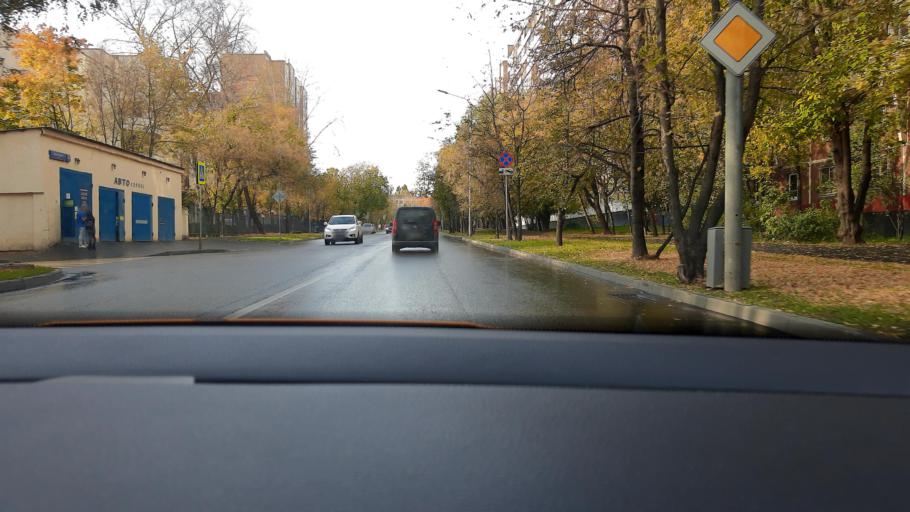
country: RU
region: Moscow
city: Metrogorodok
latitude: 55.8227
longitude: 37.7608
